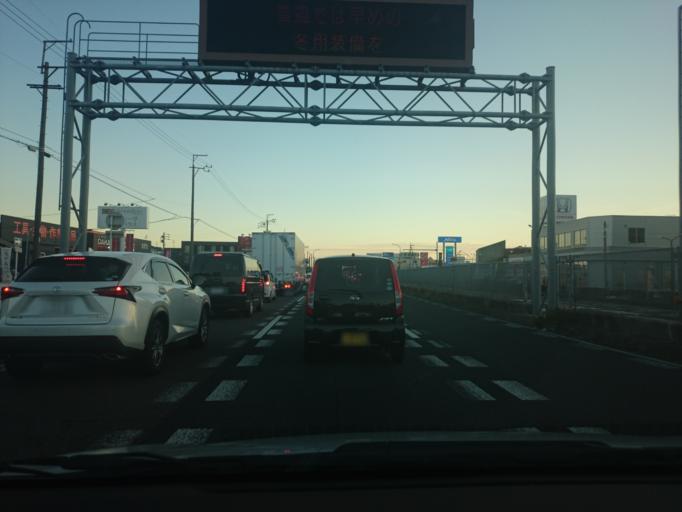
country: JP
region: Aichi
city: Ichinomiya
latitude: 35.3105
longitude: 136.8189
